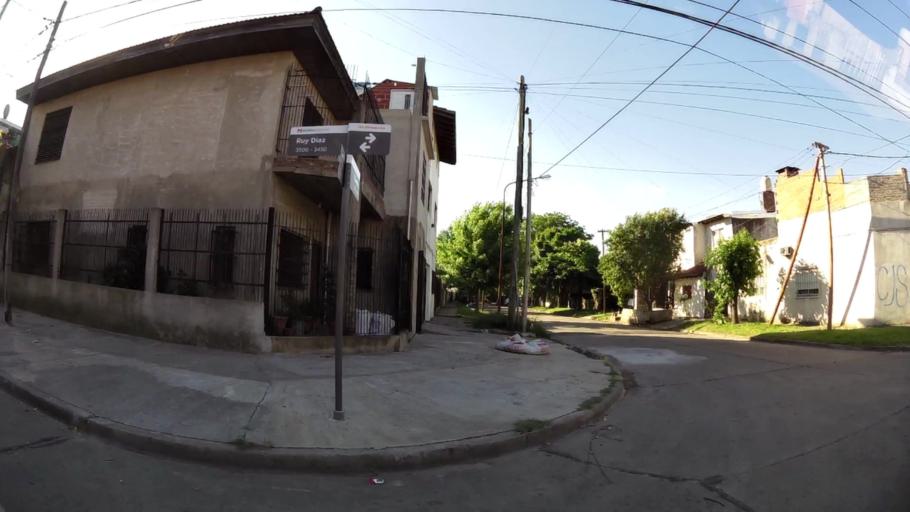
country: AR
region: Buenos Aires
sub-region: Partido de Moron
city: Moron
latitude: -34.6860
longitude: -58.6261
